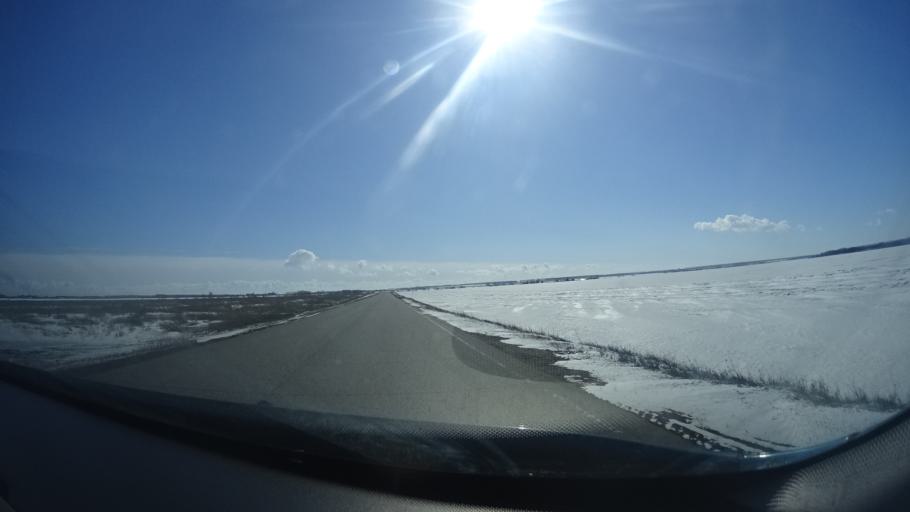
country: RU
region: Bashkortostan
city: Avdon
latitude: 54.5961
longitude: 55.8523
